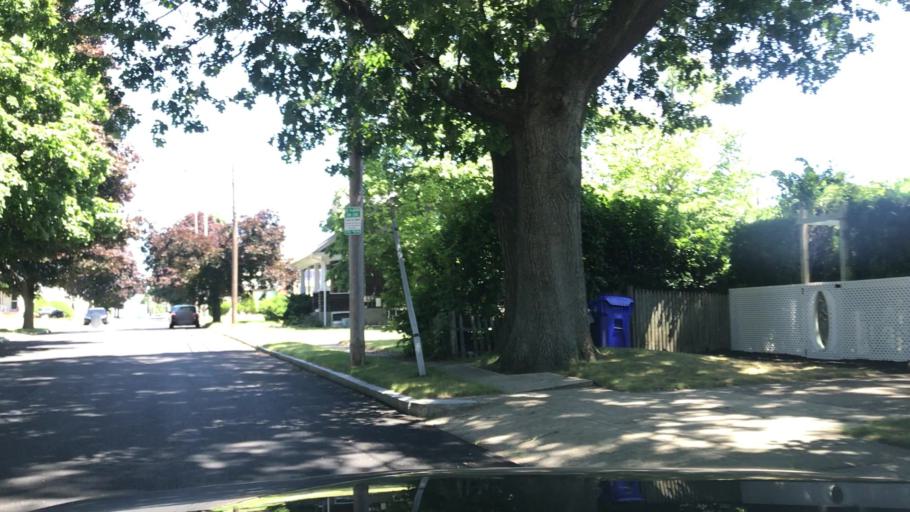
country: US
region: Rhode Island
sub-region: Providence County
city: Pawtucket
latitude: 41.8644
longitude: -71.3753
